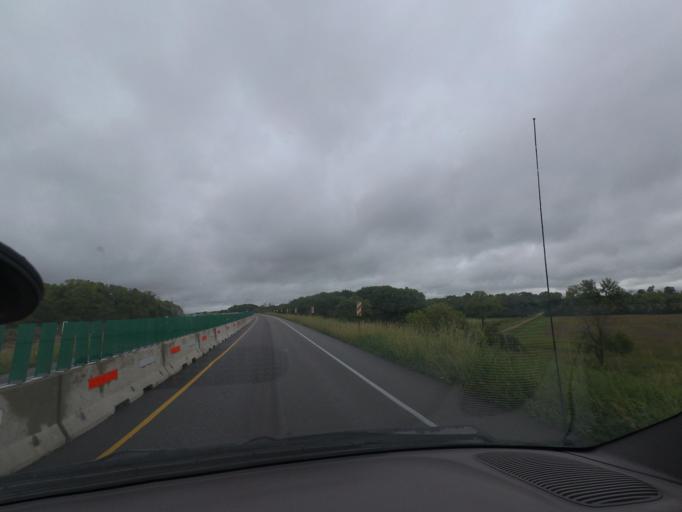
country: US
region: Illinois
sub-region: Piatt County
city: Cerro Gordo
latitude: 39.9823
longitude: -88.7906
